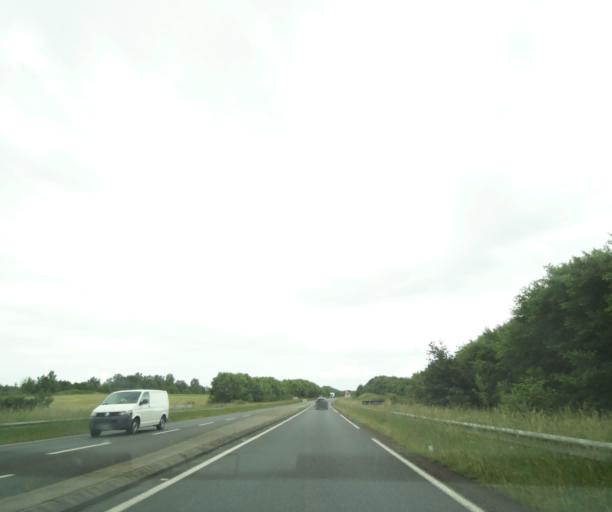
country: FR
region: Poitou-Charentes
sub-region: Departement des Deux-Sevres
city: Airvault
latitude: 46.8110
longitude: -0.2105
